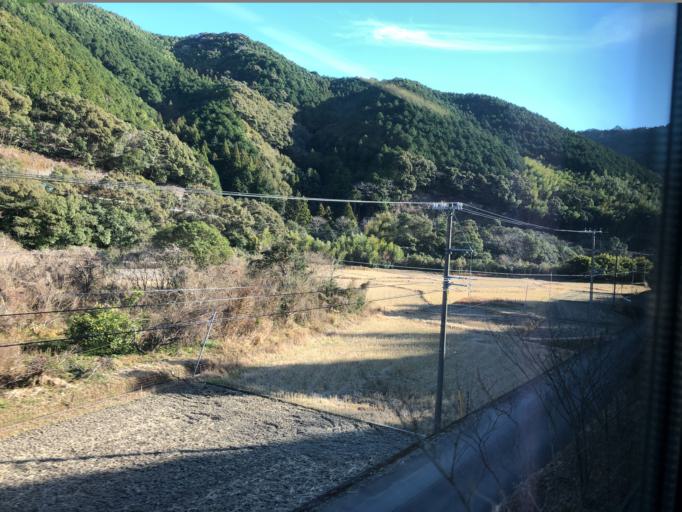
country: JP
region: Kochi
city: Nakamura
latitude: 33.1142
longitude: 133.1117
